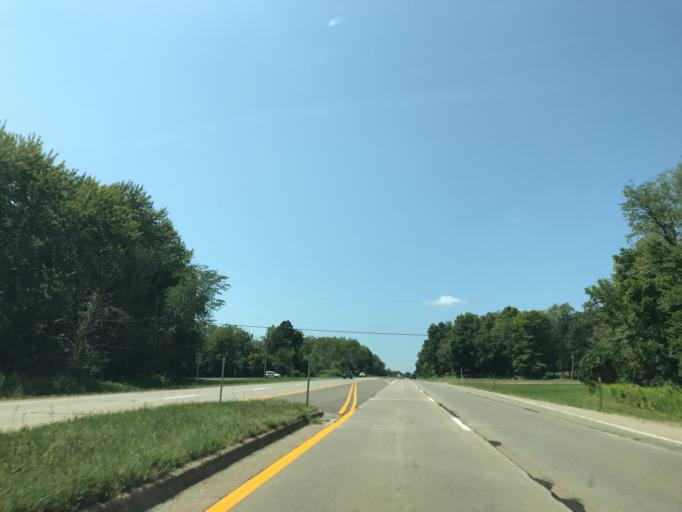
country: US
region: Michigan
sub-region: Berrien County
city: Niles
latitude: 41.8013
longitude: -86.2718
